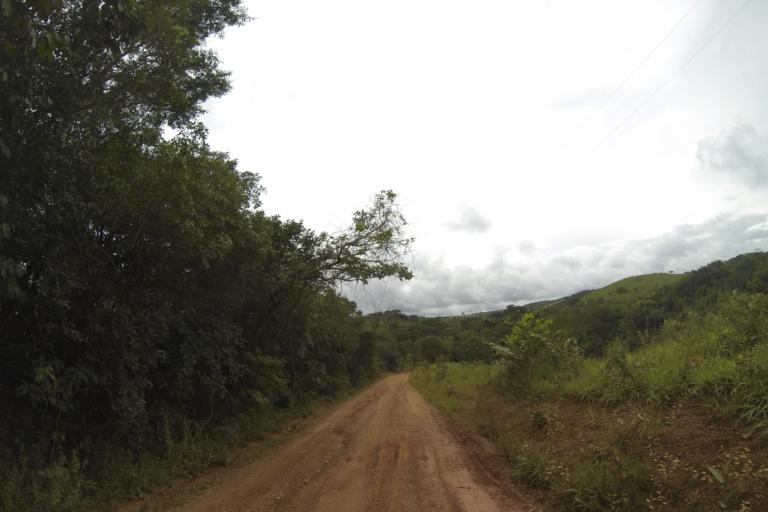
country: BR
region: Minas Gerais
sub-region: Ibia
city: Ibia
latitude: -19.7399
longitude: -46.5453
